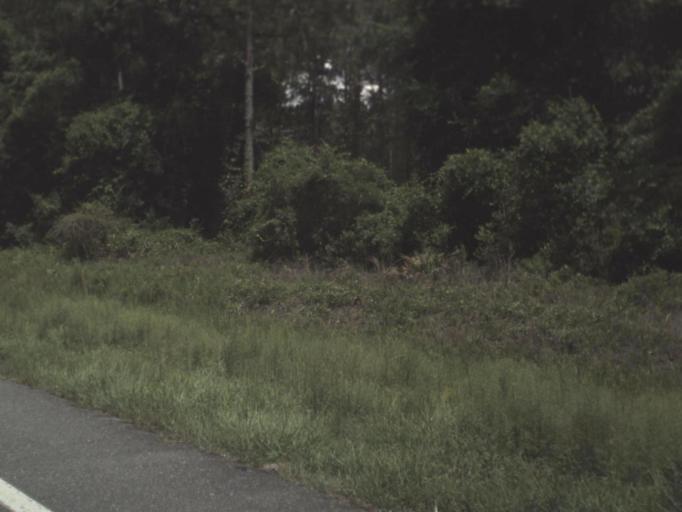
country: US
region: Florida
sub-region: Gilchrist County
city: Trenton
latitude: 29.6262
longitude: -82.7334
